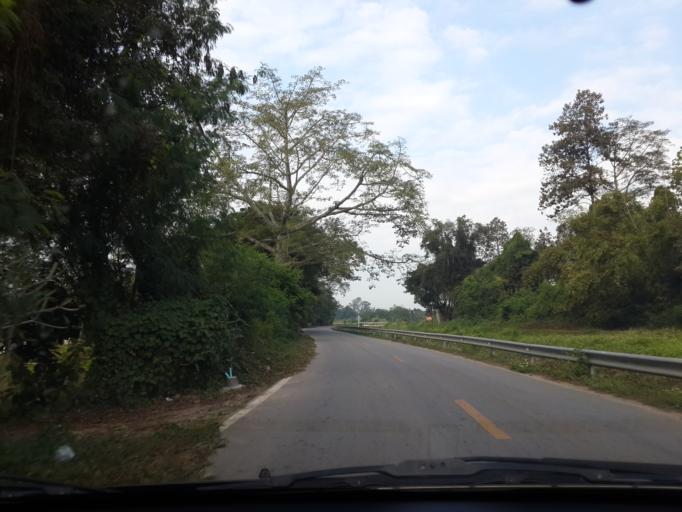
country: TH
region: Chiang Mai
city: San Sai
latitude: 18.8992
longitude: 99.0518
